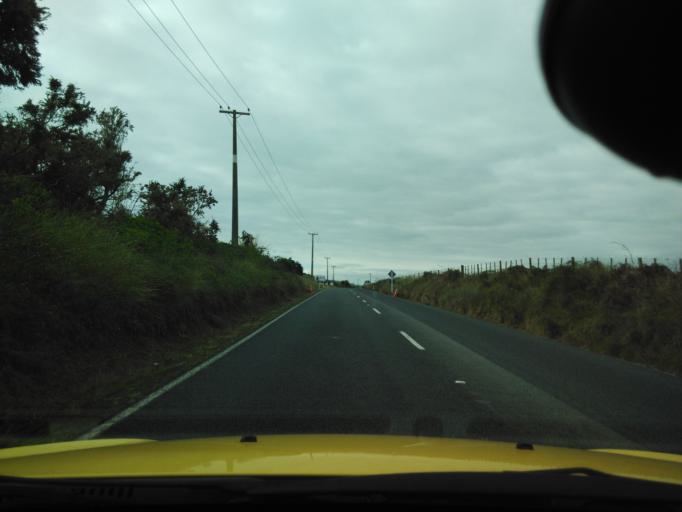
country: NZ
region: Waikato
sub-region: Waikato District
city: Ngaruawahia
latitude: -37.6306
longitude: 175.1622
